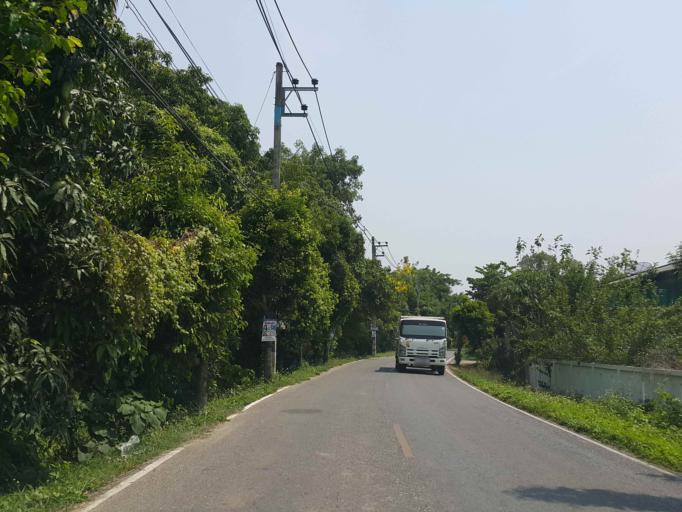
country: TH
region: Chiang Mai
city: San Sai
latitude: 18.8754
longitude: 98.9781
